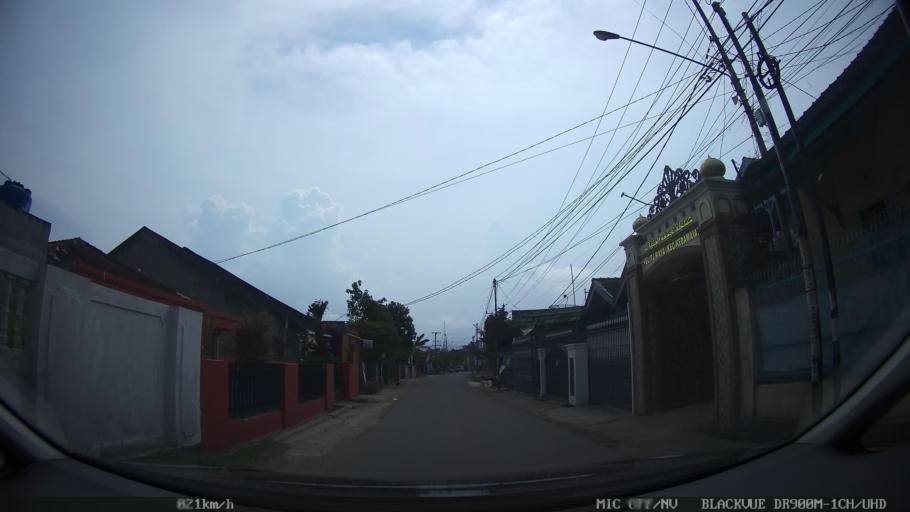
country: ID
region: Lampung
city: Bandarlampung
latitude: -5.4215
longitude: 105.2794
